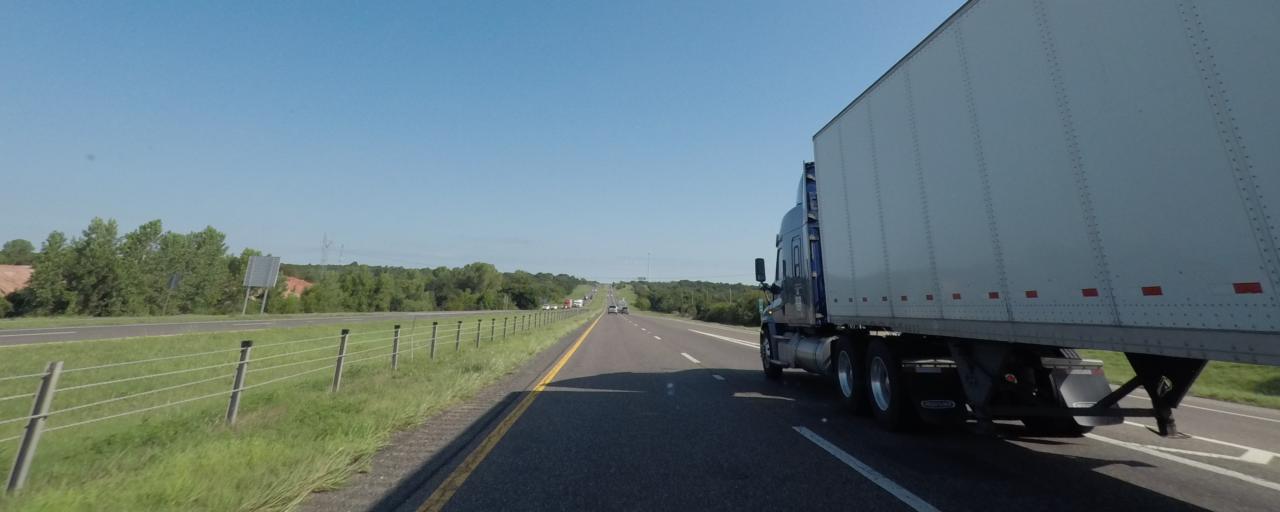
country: US
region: Oklahoma
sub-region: Oklahoma County
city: Edmond
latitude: 35.6857
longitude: -97.4162
